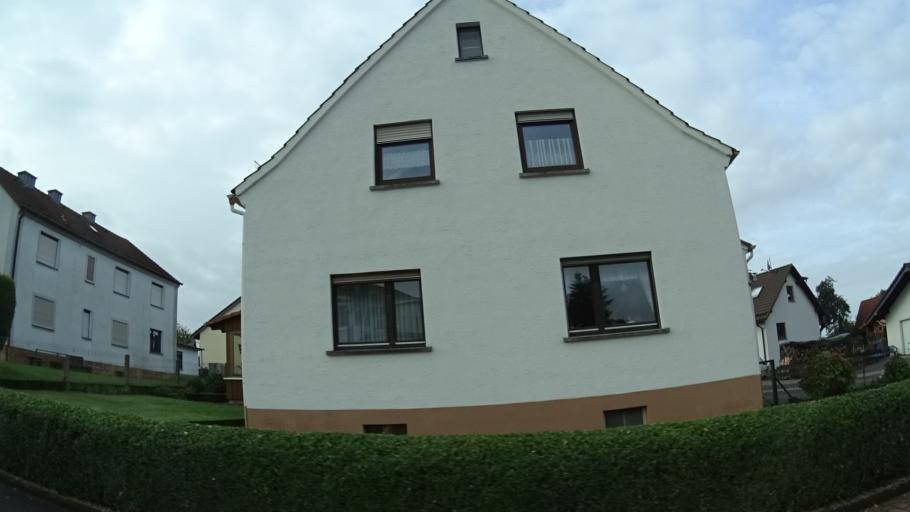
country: DE
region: Hesse
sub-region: Regierungsbezirk Kassel
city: Hofbieber
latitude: 50.5774
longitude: 9.8857
